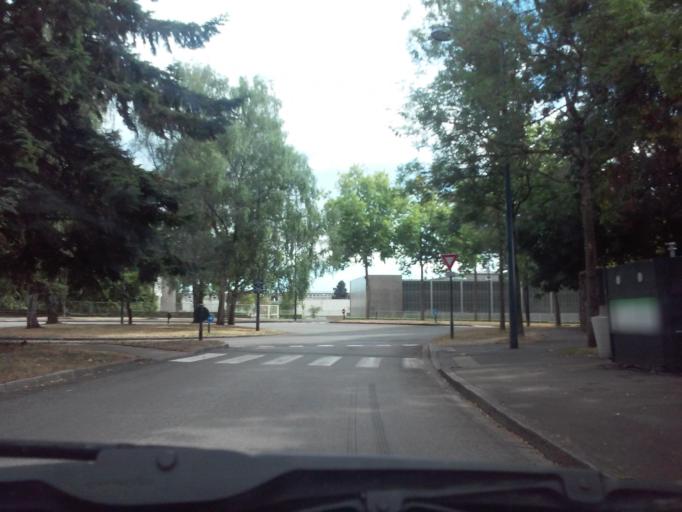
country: FR
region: Brittany
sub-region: Departement d'Ille-et-Vilaine
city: Rennes
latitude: 48.0873
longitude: -1.6855
